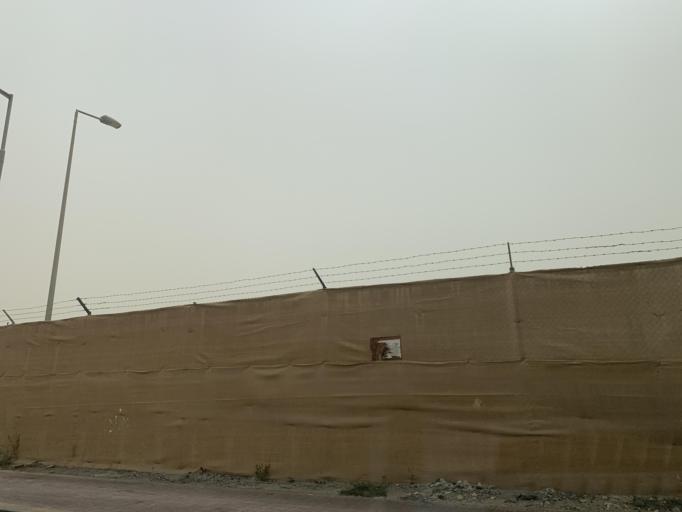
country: BH
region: Central Governorate
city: Madinat Hamad
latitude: 26.1277
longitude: 50.5128
